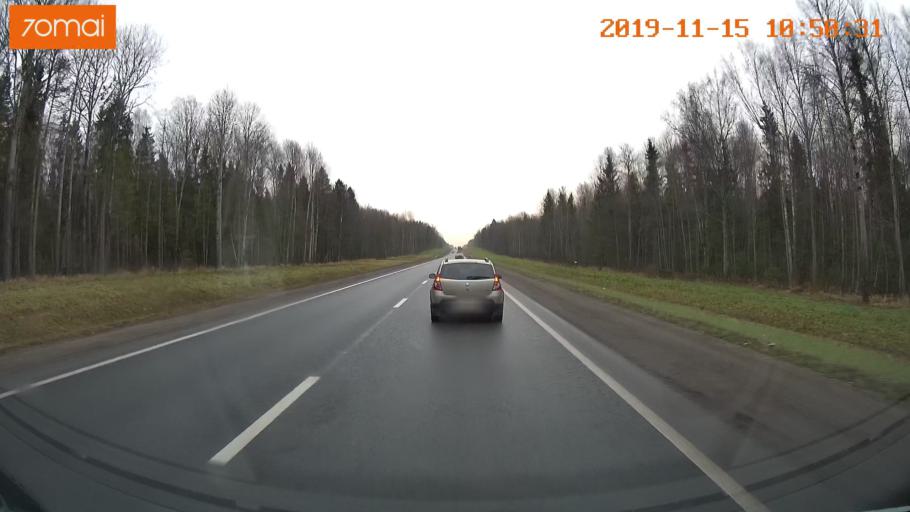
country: RU
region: Vologda
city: Chebsara
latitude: 59.1849
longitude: 38.6832
